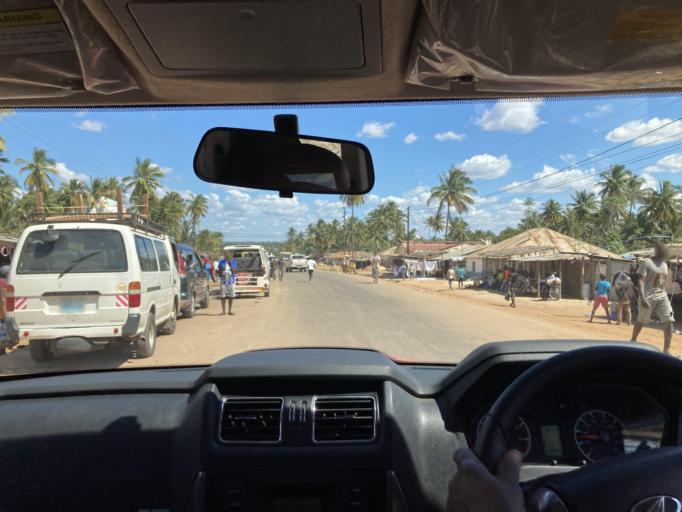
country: MZ
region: Cabo Delgado
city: Montepuez
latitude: -13.1317
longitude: 38.9940
